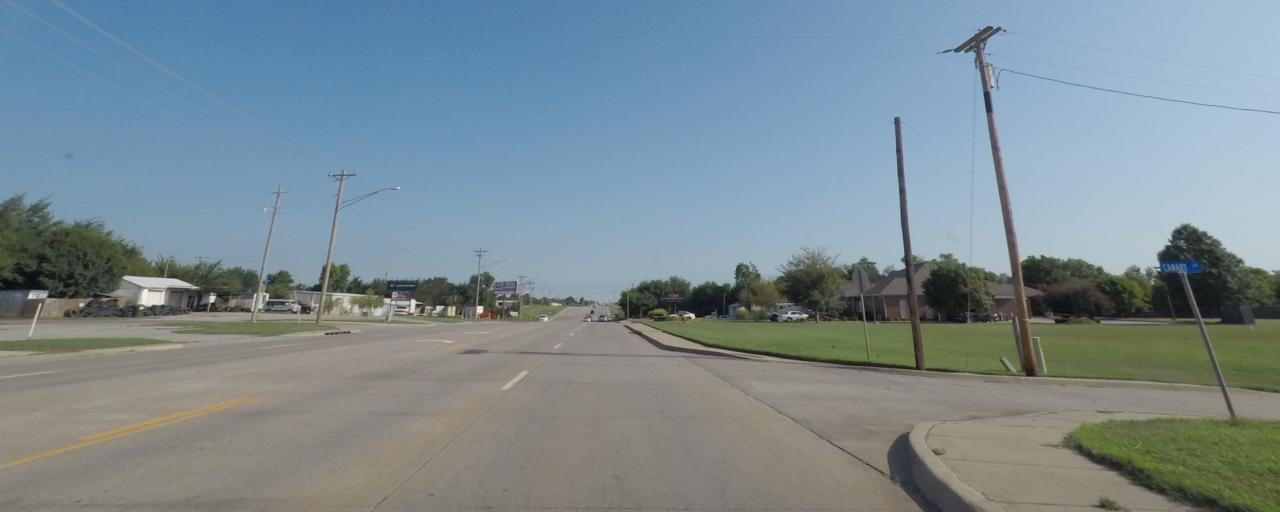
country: US
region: Oklahoma
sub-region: McClain County
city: Newcastle
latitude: 35.2595
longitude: -97.6001
